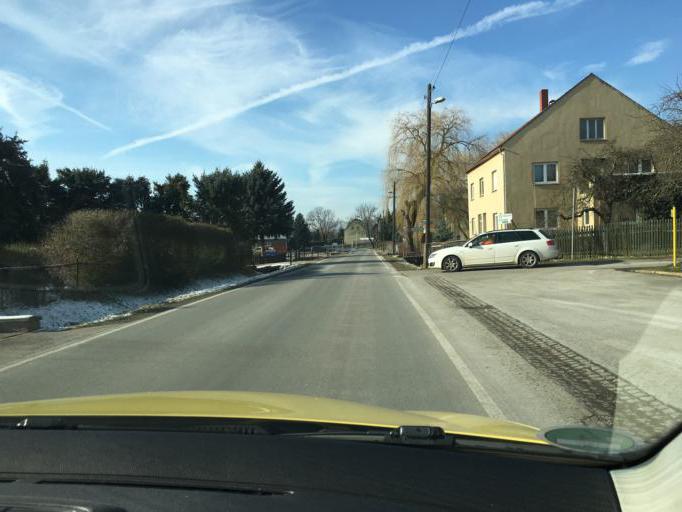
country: DE
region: Saxony
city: Narsdorf
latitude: 50.9907
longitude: 12.7050
